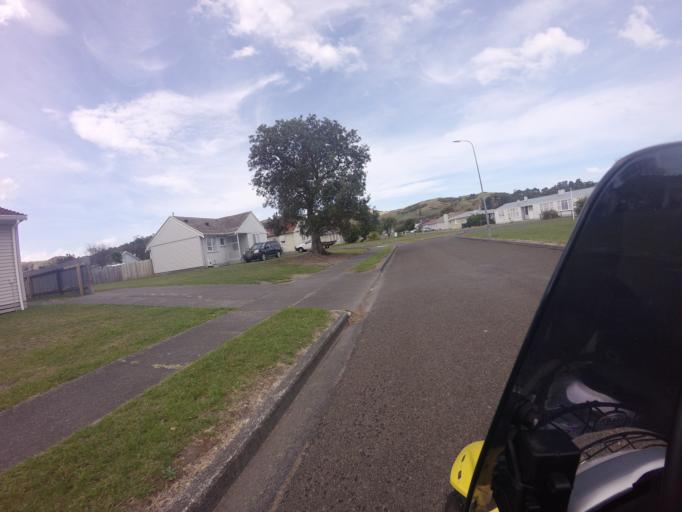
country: NZ
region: Gisborne
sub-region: Gisborne District
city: Gisborne
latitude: -38.6729
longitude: 178.0524
